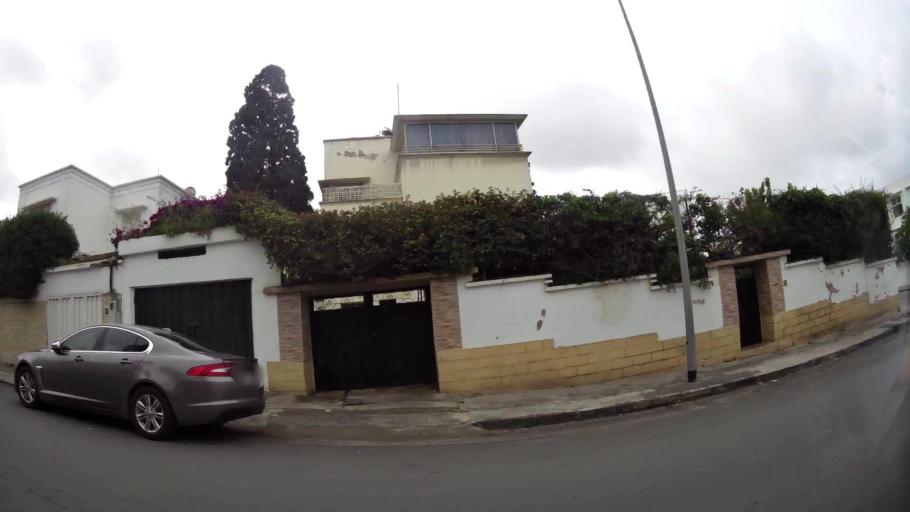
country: MA
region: Grand Casablanca
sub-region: Casablanca
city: Casablanca
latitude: 33.5817
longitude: -7.6098
